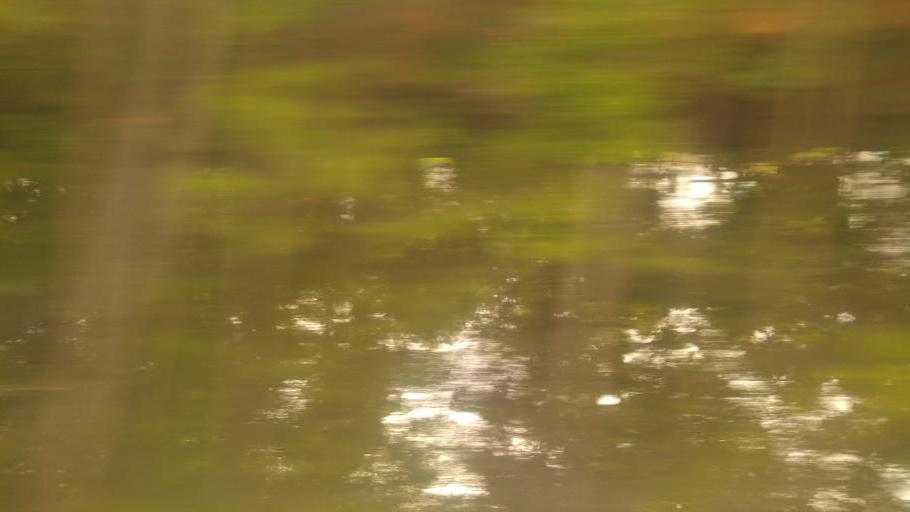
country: US
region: Virginia
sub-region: Henrico County
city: Glen Allen
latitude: 37.6707
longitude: -77.5041
